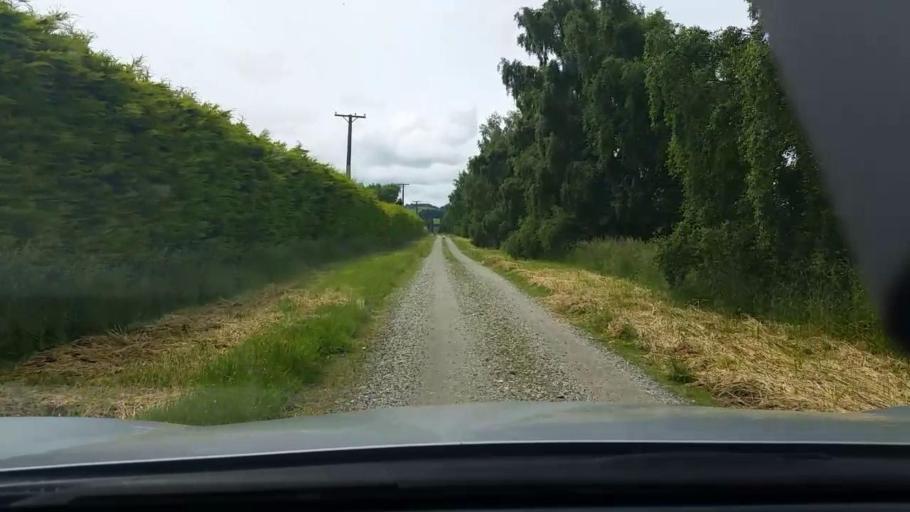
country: NZ
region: Southland
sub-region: Gore District
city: Gore
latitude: -46.1230
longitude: 168.9285
